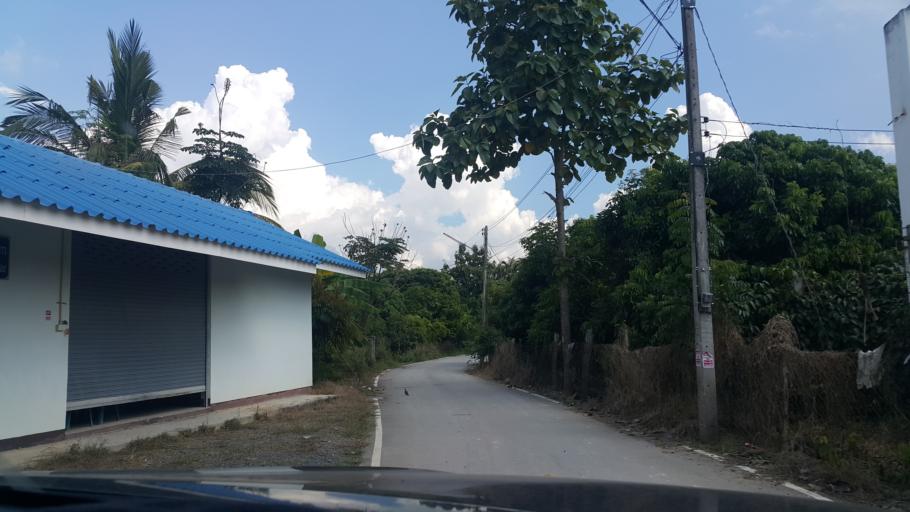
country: TH
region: Chiang Mai
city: San Kamphaeng
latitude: 18.7212
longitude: 99.1711
